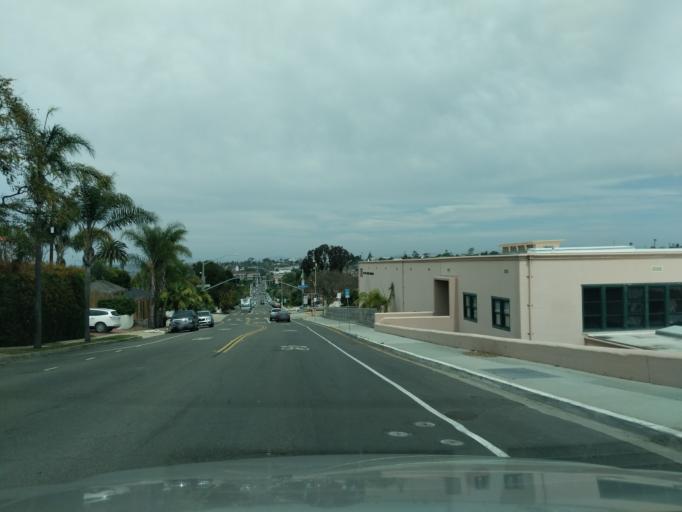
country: US
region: California
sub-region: San Diego County
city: Coronado
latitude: 32.7331
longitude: -117.2343
